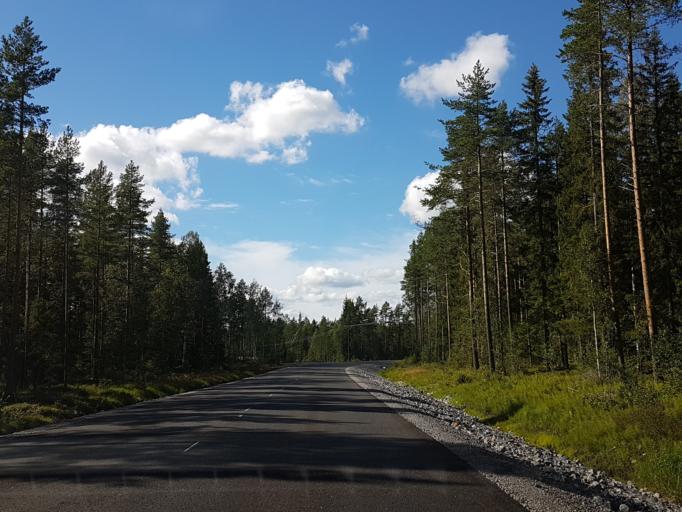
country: SE
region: Vaesterbotten
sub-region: Robertsfors Kommun
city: Robertsfors
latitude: 64.1290
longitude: 20.6466
